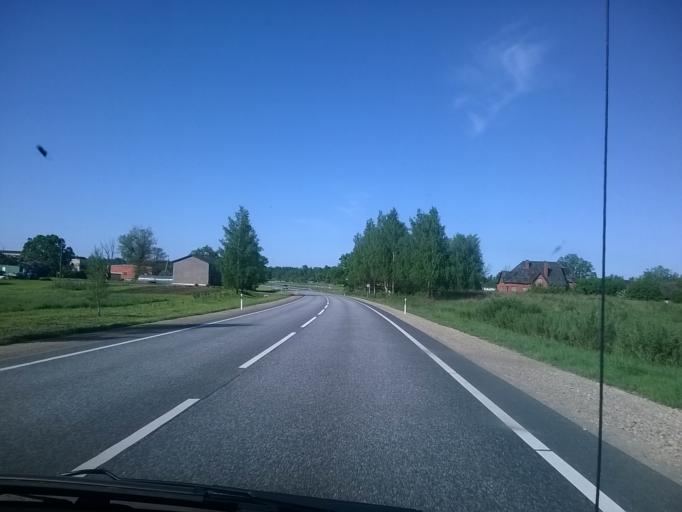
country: LV
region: Valmieras Rajons
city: Valmiera
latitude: 57.5497
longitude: 25.3926
